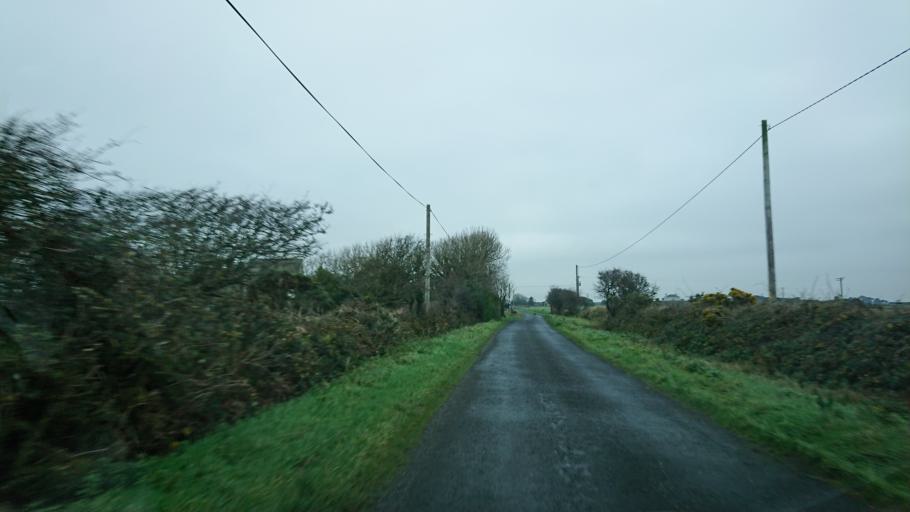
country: IE
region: Munster
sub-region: Waterford
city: Dunmore East
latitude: 52.1555
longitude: -7.0426
